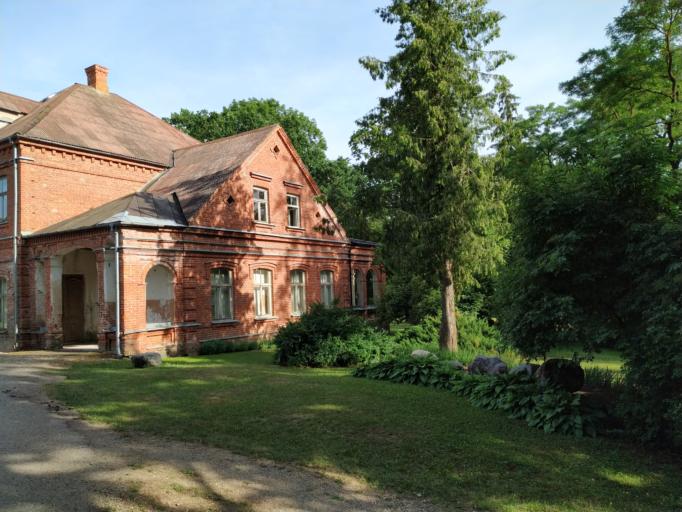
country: LT
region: Panevezys
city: Pasvalys
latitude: 56.1067
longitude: 24.4957
